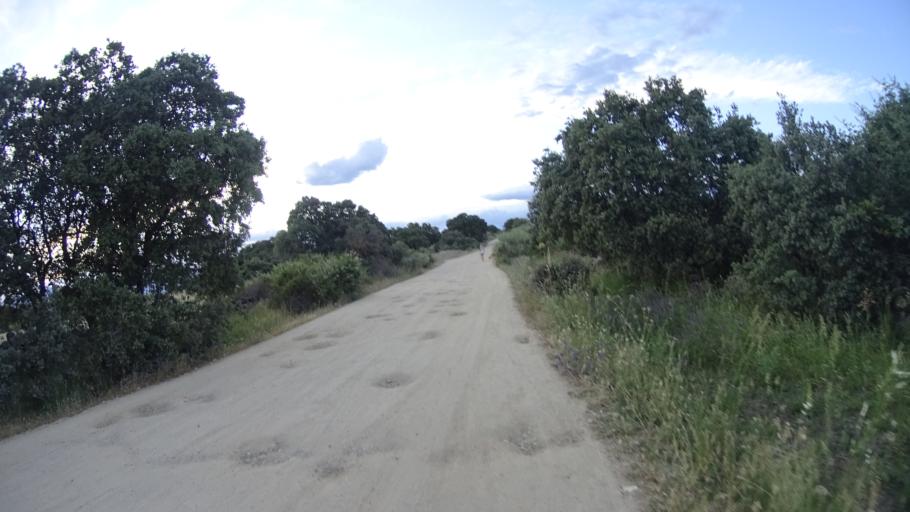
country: ES
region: Madrid
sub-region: Provincia de Madrid
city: Colmenarejo
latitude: 40.5384
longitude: -4.0097
